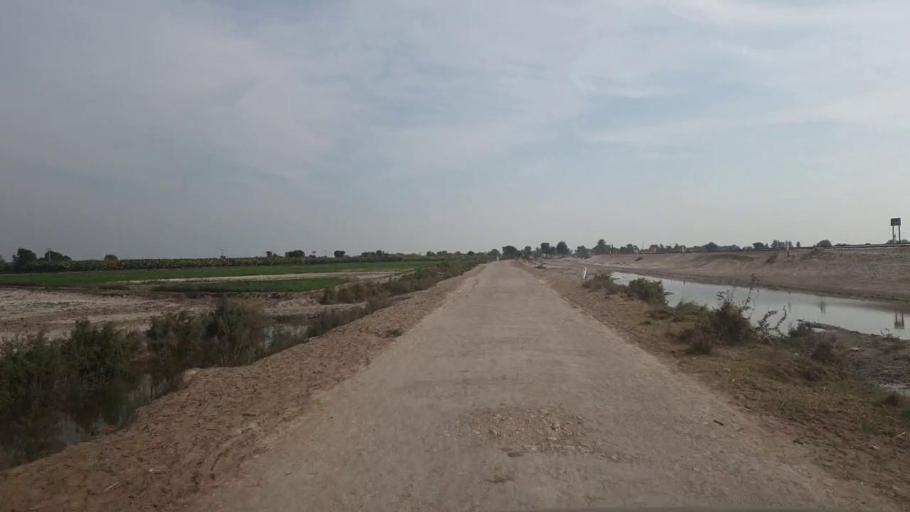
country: PK
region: Sindh
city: Shahpur Chakar
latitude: 26.0865
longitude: 68.4878
